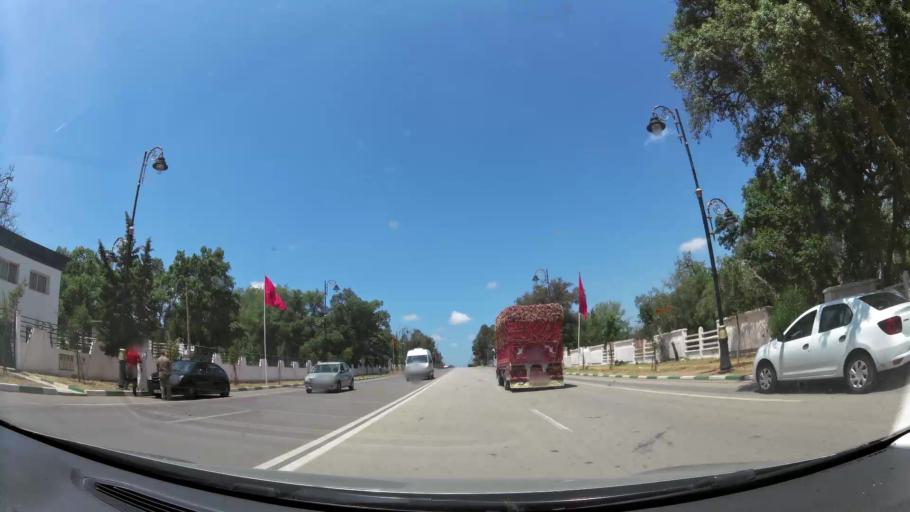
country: MA
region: Gharb-Chrarda-Beni Hssen
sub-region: Kenitra Province
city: Kenitra
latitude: 34.2433
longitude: -6.5727
